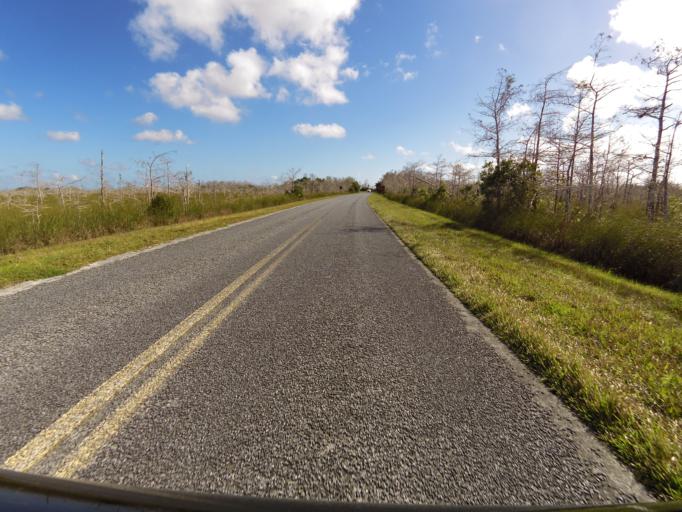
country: US
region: Florida
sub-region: Miami-Dade County
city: Florida City
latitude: 25.4295
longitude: -80.7725
